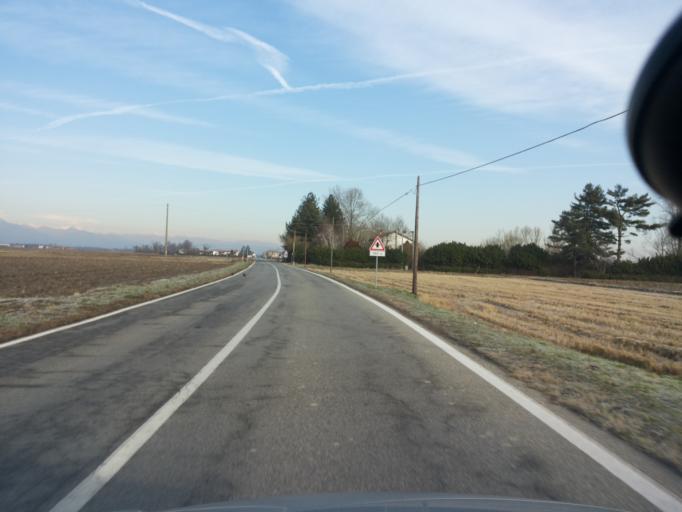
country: IT
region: Piedmont
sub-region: Provincia di Vercelli
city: Oldenico
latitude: 45.3942
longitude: 8.3795
